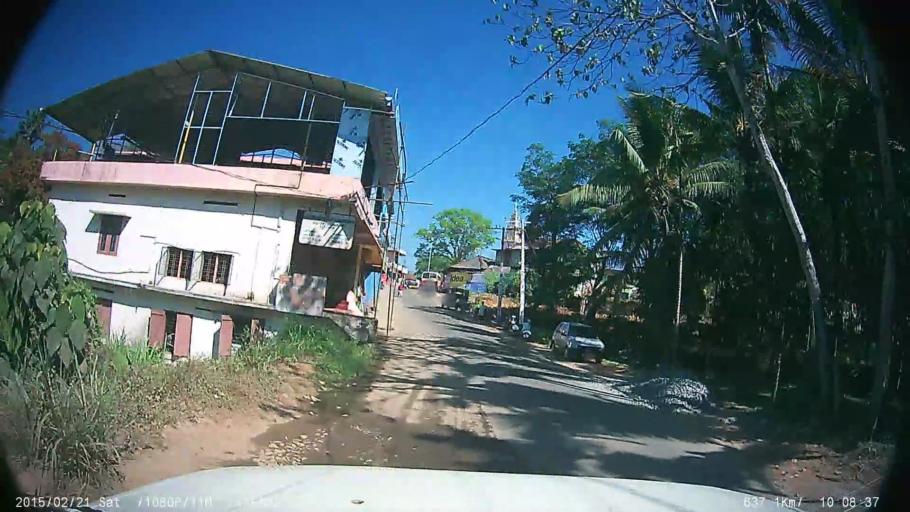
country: IN
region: Kerala
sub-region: Ernakulam
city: Muvattupuzha
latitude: 9.8801
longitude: 76.6059
